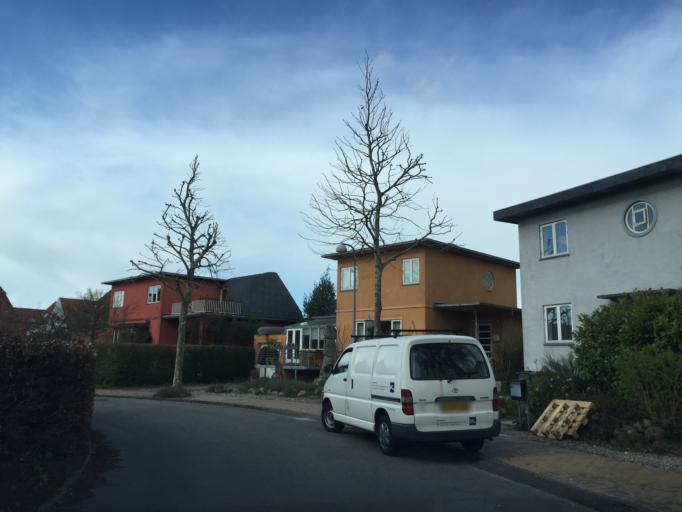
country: DK
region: South Denmark
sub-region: Odense Kommune
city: Odense
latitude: 55.3878
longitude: 10.3999
